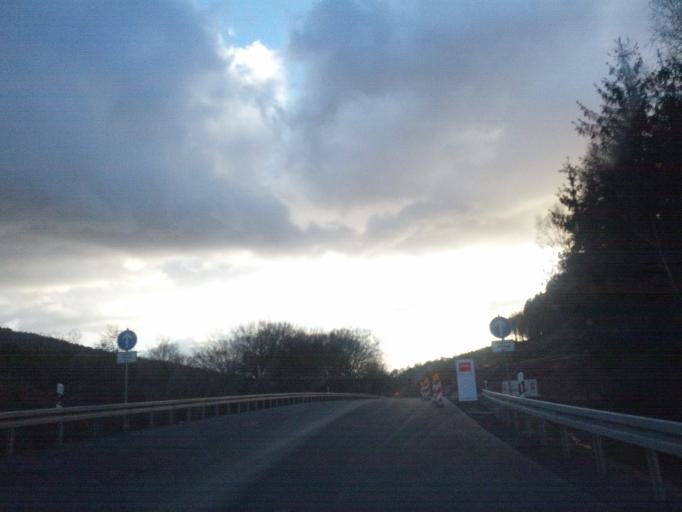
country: DE
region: Hesse
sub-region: Regierungsbezirk Kassel
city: Helsa
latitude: 51.2454
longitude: 9.6827
